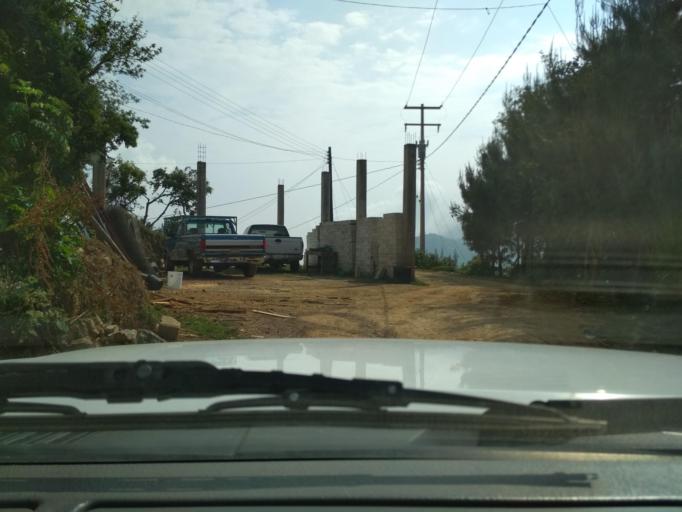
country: MX
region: Veracruz
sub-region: Soledad Atzompa
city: Tlatilpa
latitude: 18.7524
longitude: -97.1521
